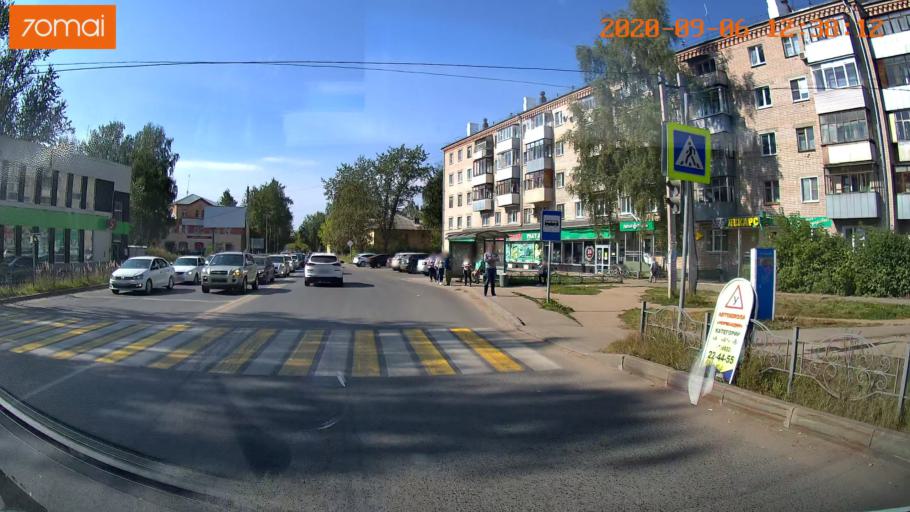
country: RU
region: Ivanovo
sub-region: Gorod Ivanovo
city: Ivanovo
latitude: 57.0306
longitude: 40.9804
